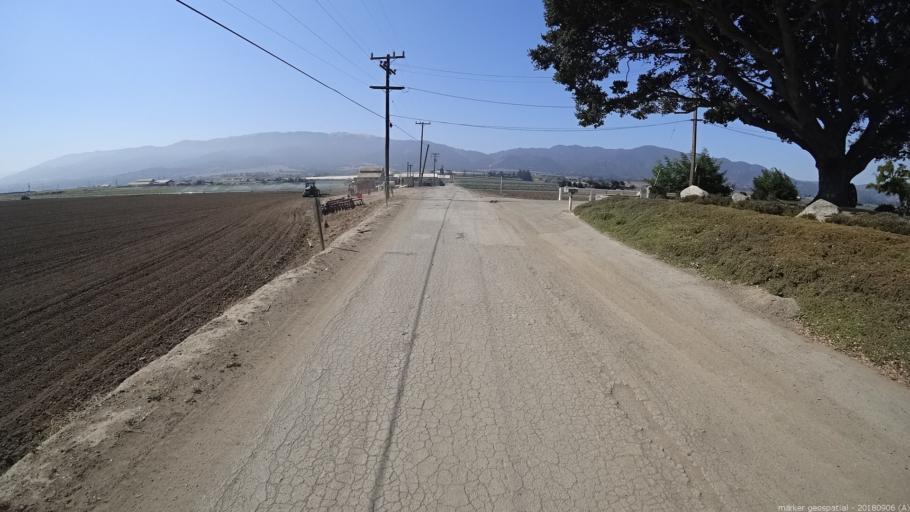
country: US
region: California
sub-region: Monterey County
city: Chualar
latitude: 36.6007
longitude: -121.6030
